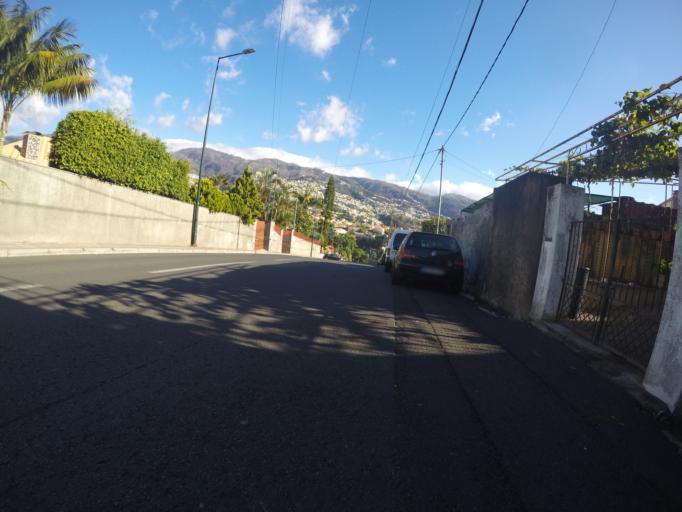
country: PT
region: Madeira
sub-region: Funchal
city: Nossa Senhora do Monte
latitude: 32.6532
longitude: -16.9233
